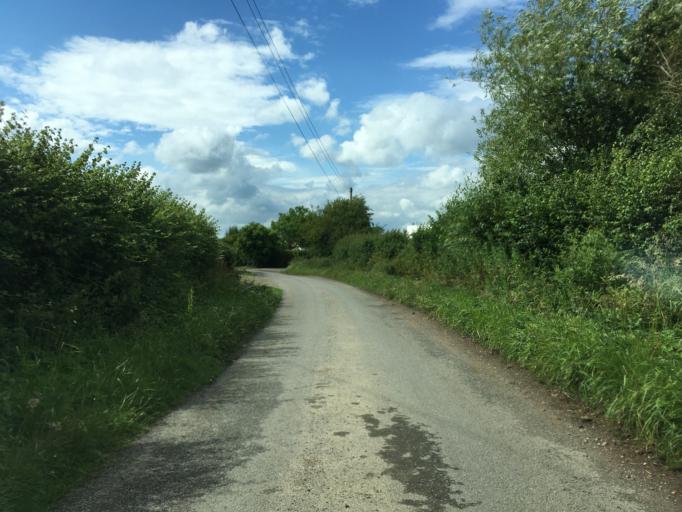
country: GB
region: England
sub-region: Gloucestershire
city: Gloucester
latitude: 51.8360
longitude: -2.3330
